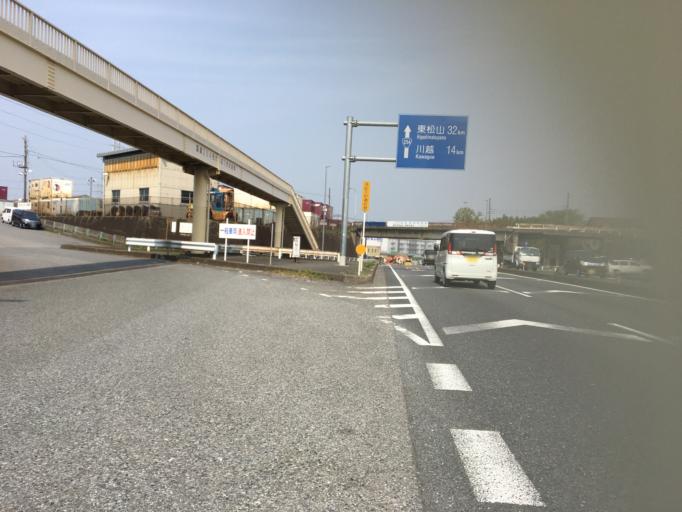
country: JP
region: Saitama
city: Shiki
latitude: 35.8038
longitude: 139.5539
